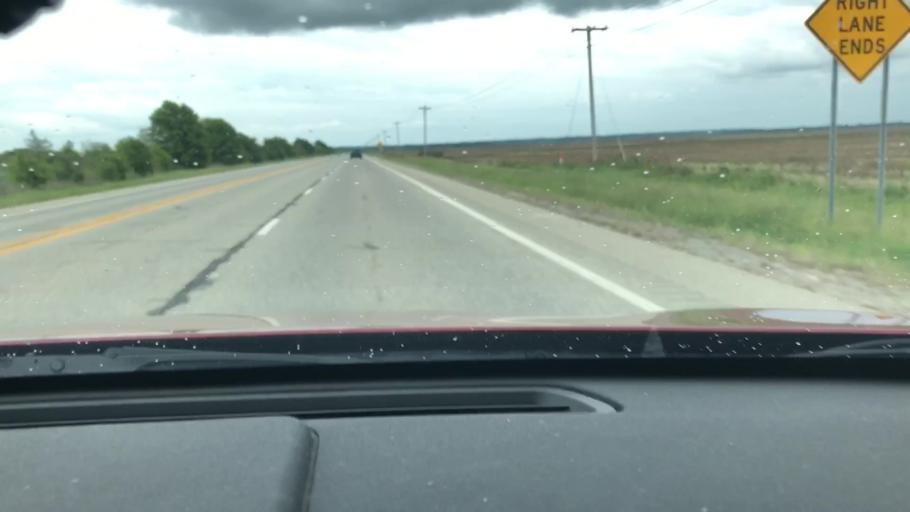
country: US
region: Arkansas
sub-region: Lafayette County
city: Lewisville
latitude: 33.4121
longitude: -93.7826
